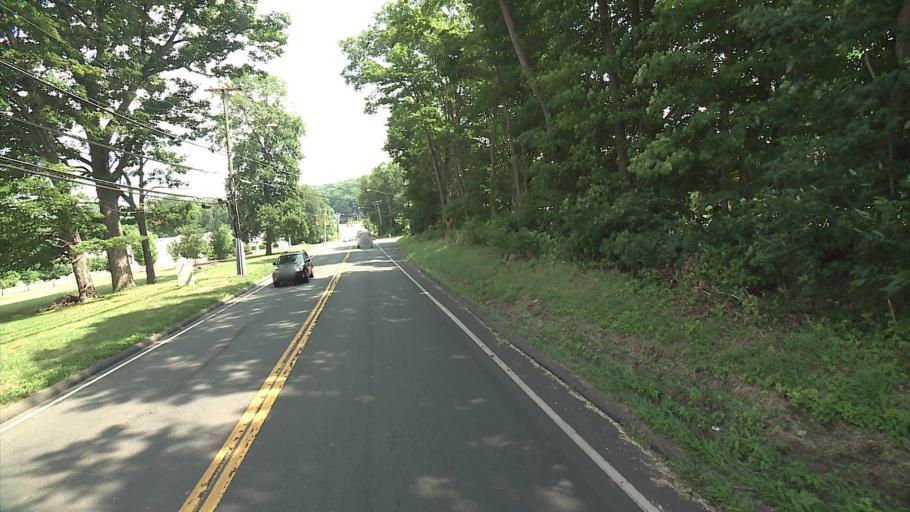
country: US
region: Connecticut
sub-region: Middlesex County
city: Cromwell
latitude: 41.5979
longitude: -72.6954
